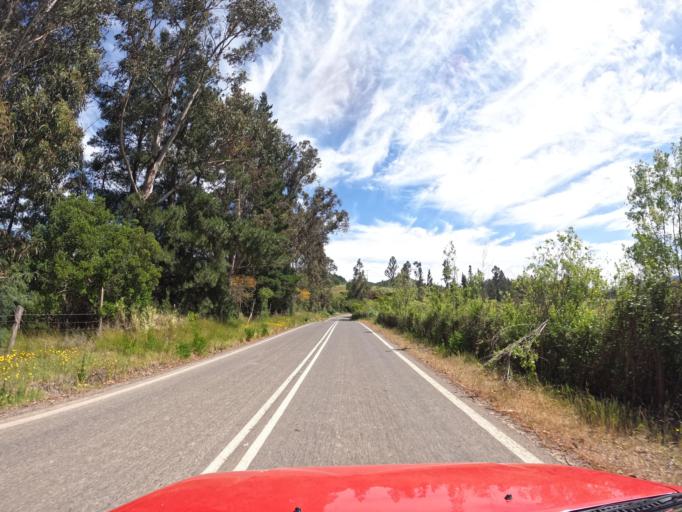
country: CL
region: Maule
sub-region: Provincia de Talca
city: Talca
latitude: -34.9925
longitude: -71.8593
